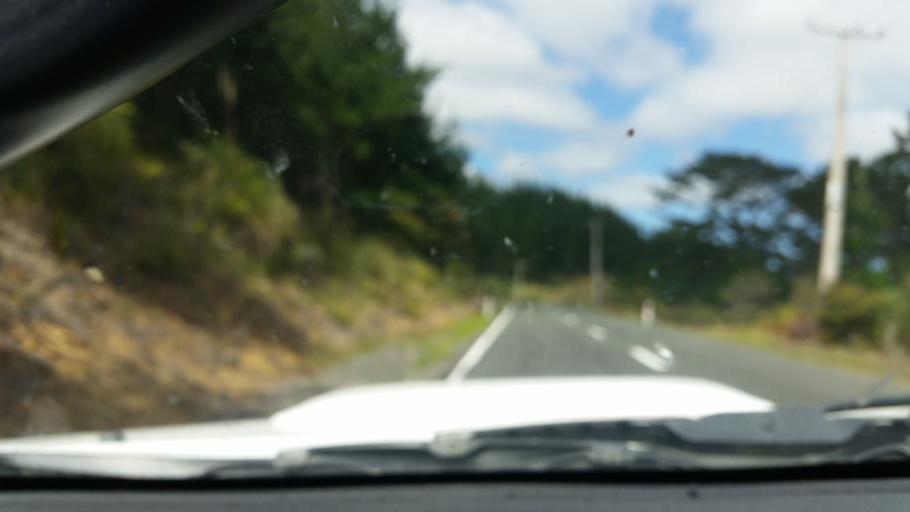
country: NZ
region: Northland
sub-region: Kaipara District
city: Dargaville
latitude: -35.8153
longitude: 173.7189
